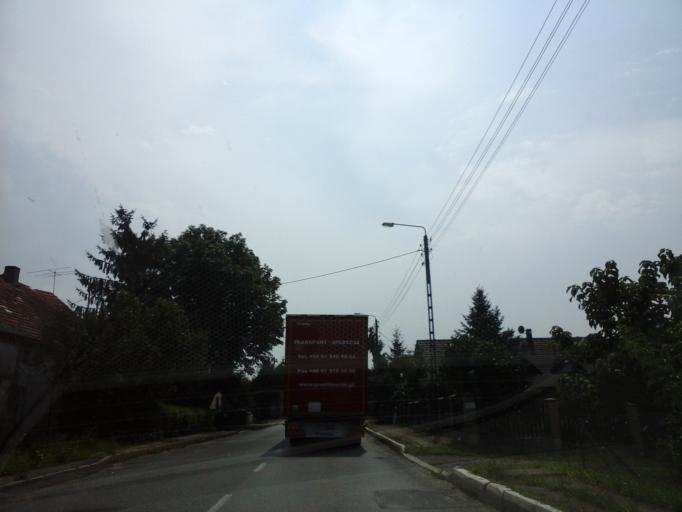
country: PL
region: Lower Silesian Voivodeship
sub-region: Powiat wroclawski
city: Zorawina
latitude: 50.9143
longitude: 17.0665
